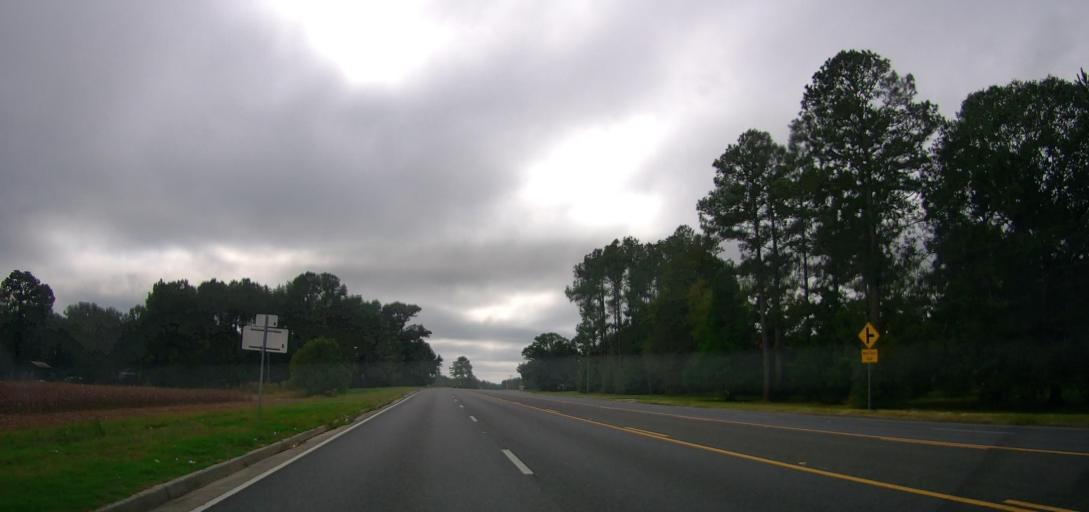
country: US
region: Georgia
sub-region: Colquitt County
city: Moultrie
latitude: 31.0732
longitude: -83.8225
